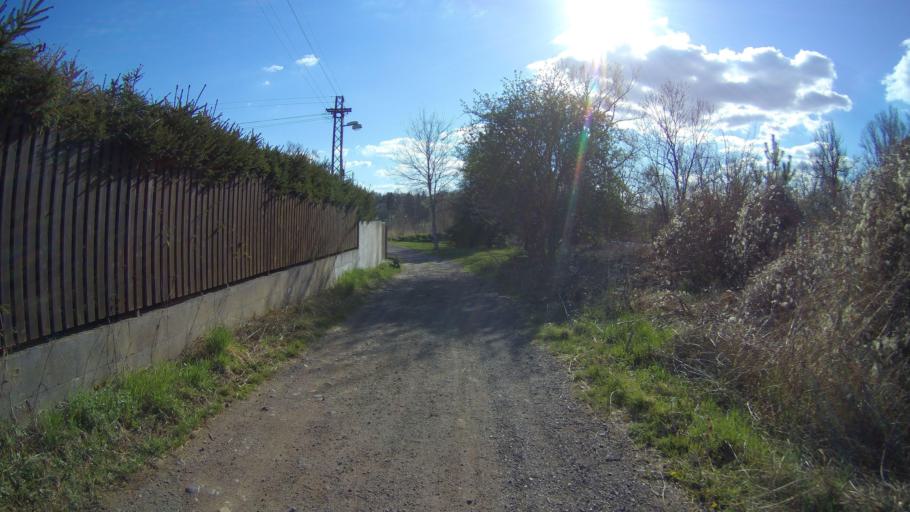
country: CZ
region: Ustecky
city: Zatec
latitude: 50.3331
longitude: 13.5198
